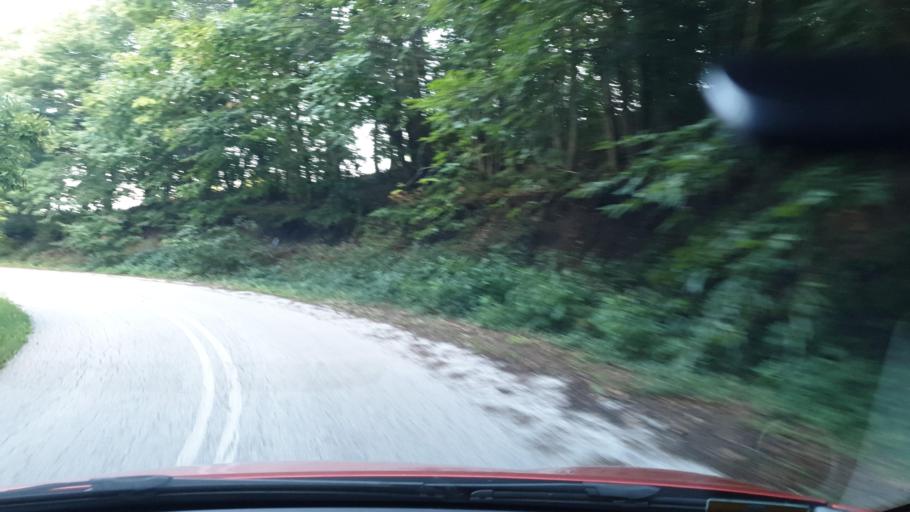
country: GR
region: Central Macedonia
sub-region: Nomos Chalkidikis
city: Galatista
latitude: 40.5071
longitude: 23.2614
